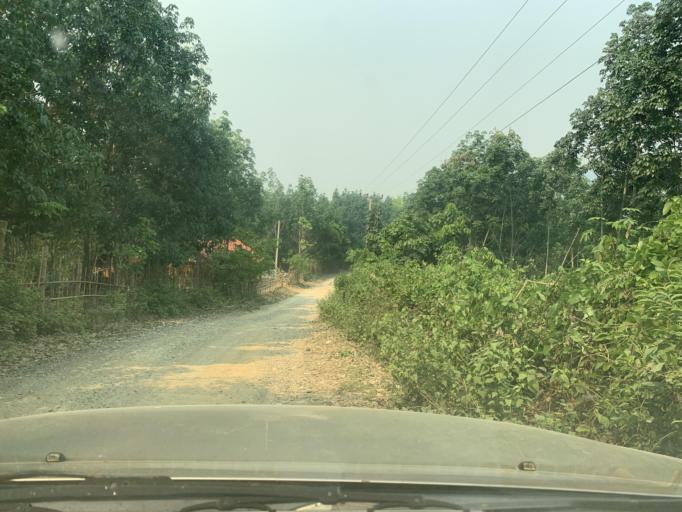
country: LA
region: Louangphabang
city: Louangphabang
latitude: 19.8949
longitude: 102.2527
